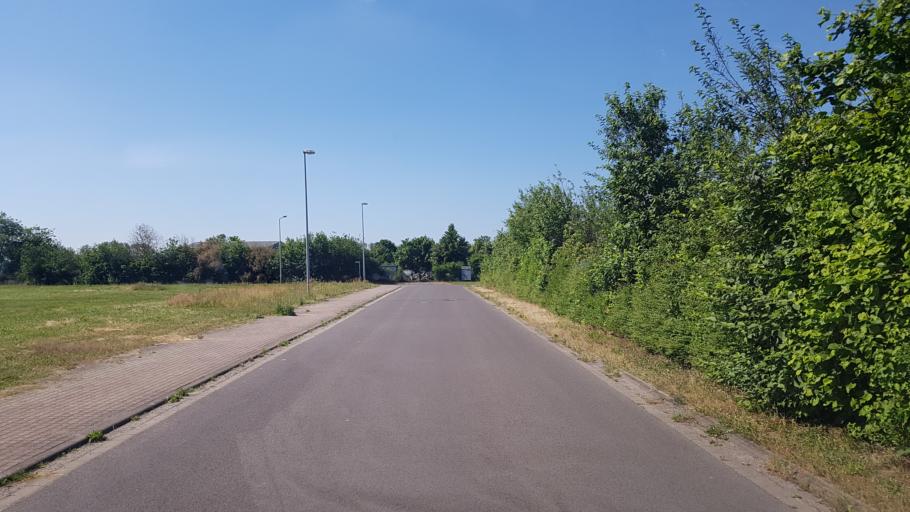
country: DE
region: Brandenburg
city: Plessa
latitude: 51.4672
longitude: 13.6073
